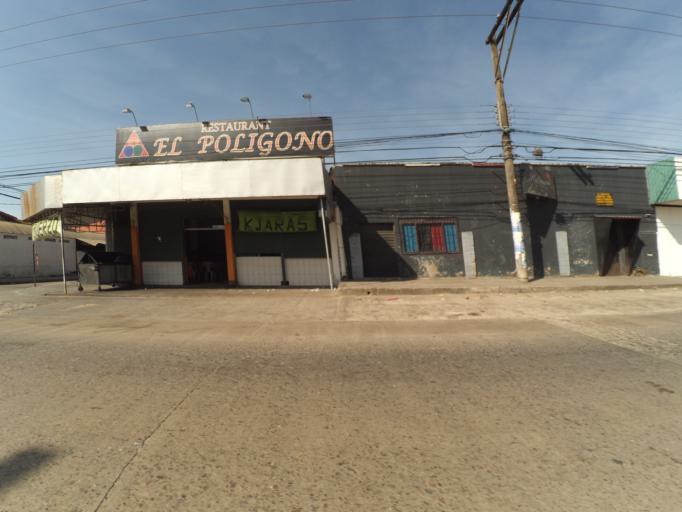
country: BO
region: Santa Cruz
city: Santa Cruz de la Sierra
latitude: -17.8163
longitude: -63.2027
